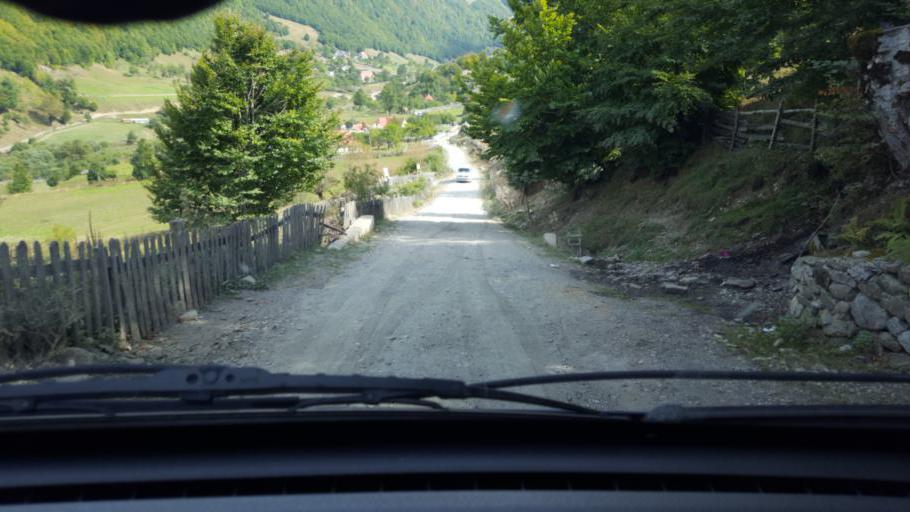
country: AL
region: Kukes
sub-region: Rrethi i Tropojes
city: Valbone
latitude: 42.5305
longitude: 19.7235
